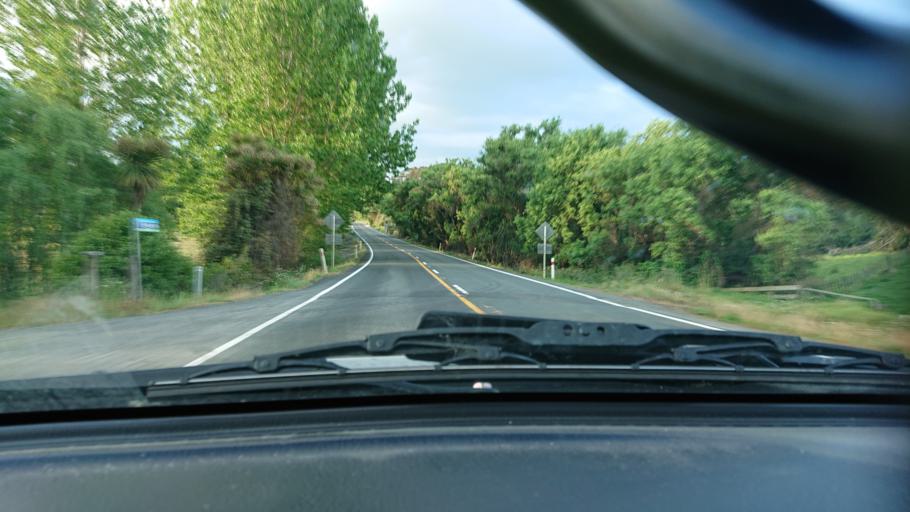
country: NZ
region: Auckland
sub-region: Auckland
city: Parakai
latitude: -36.5343
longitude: 174.4567
